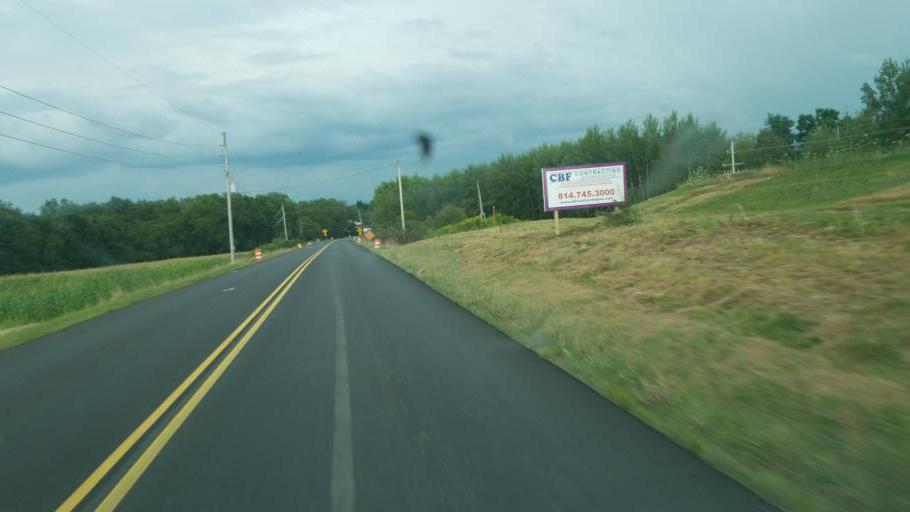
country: US
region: Pennsylvania
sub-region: Clarion County
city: Knox
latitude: 41.2407
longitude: -79.5325
